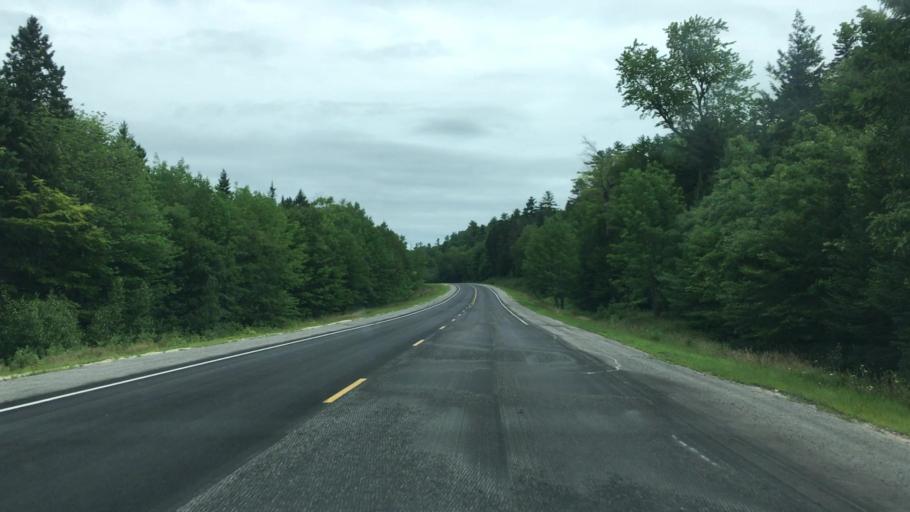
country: US
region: Maine
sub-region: Washington County
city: Cherryfield
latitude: 44.8959
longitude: -67.8558
